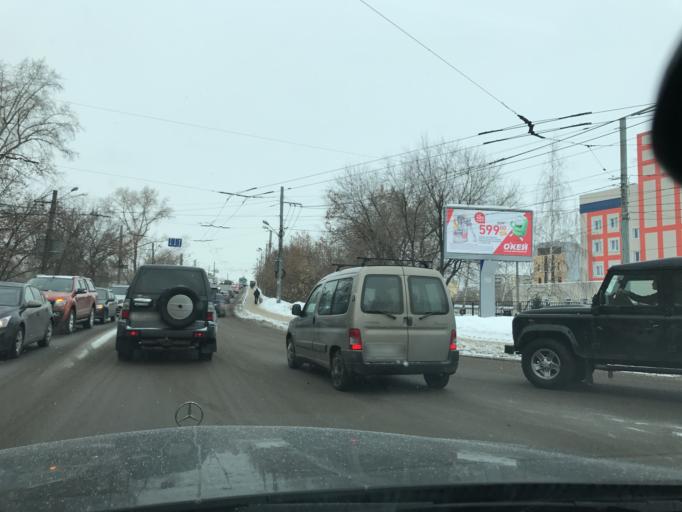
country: RU
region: Nizjnij Novgorod
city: Nizhniy Novgorod
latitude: 56.3263
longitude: 43.9533
